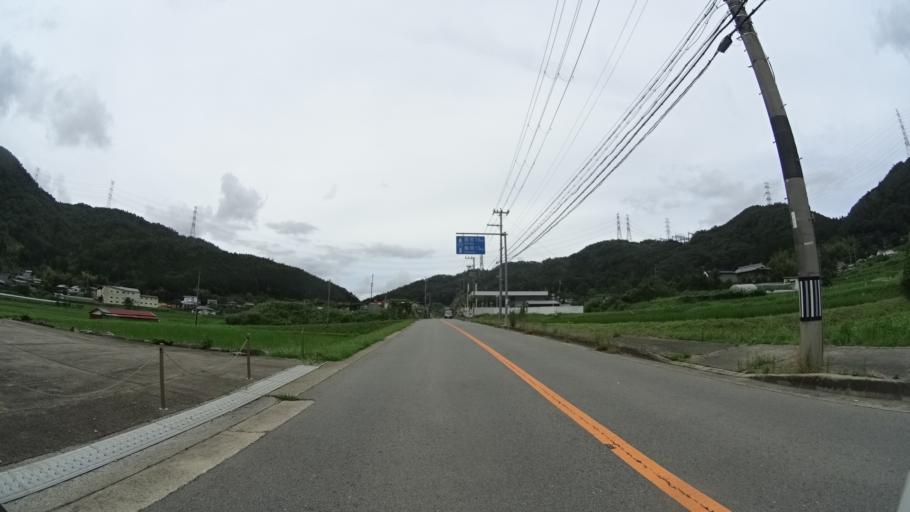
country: JP
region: Kyoto
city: Kameoka
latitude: 34.9858
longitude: 135.4743
